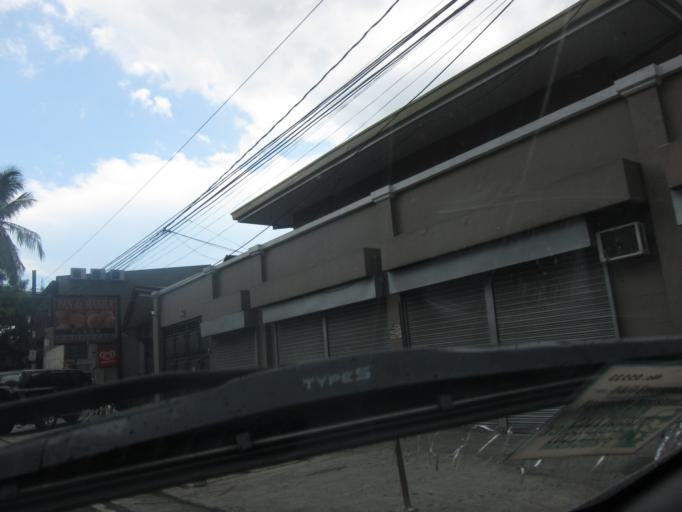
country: PH
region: Metro Manila
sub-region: Quezon City
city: Quezon City
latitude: 14.6403
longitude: 121.0547
